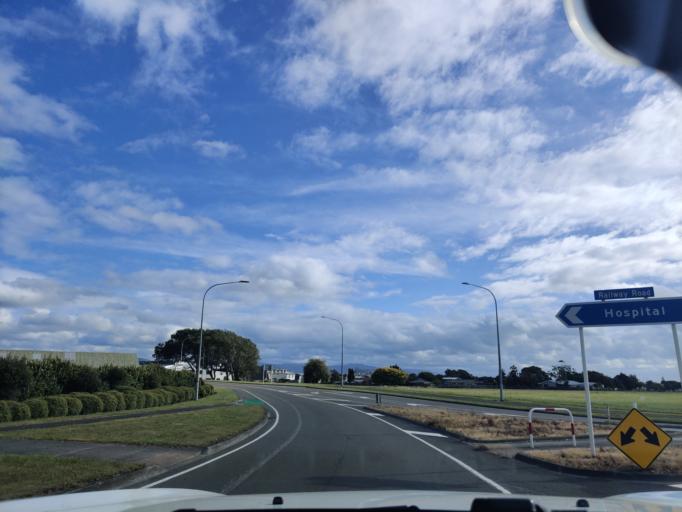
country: NZ
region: Manawatu-Wanganui
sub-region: Palmerston North City
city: Palmerston North
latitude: -40.3246
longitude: 175.6255
